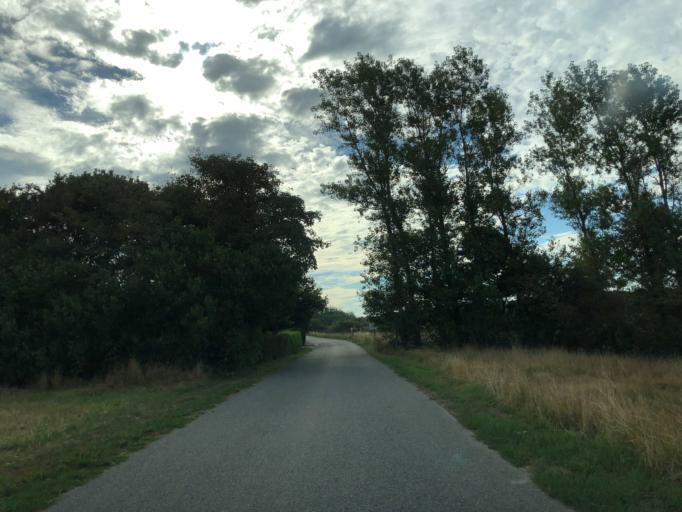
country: DK
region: Central Jutland
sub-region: Ringkobing-Skjern Kommune
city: Skjern
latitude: 56.0447
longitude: 8.4203
